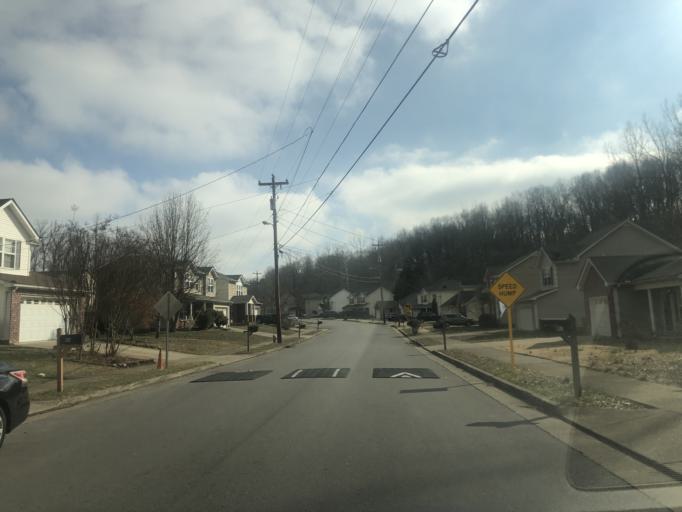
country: US
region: Tennessee
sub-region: Rutherford County
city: La Vergne
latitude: 36.0763
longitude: -86.6559
